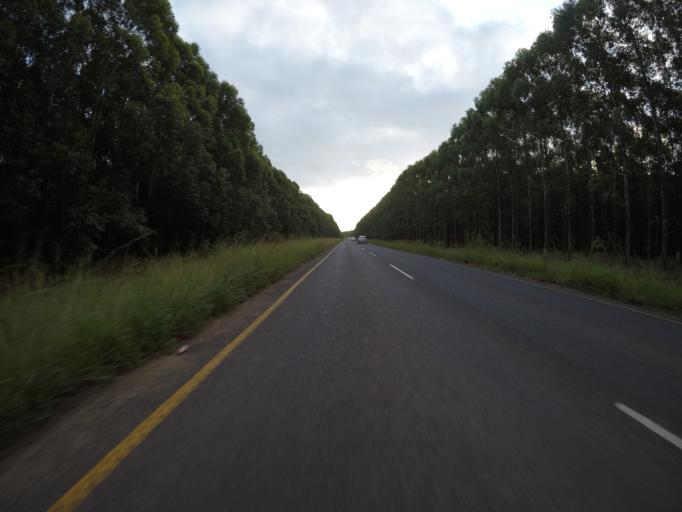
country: ZA
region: KwaZulu-Natal
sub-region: uMkhanyakude District Municipality
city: Mtubatuba
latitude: -28.3992
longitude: 32.2119
